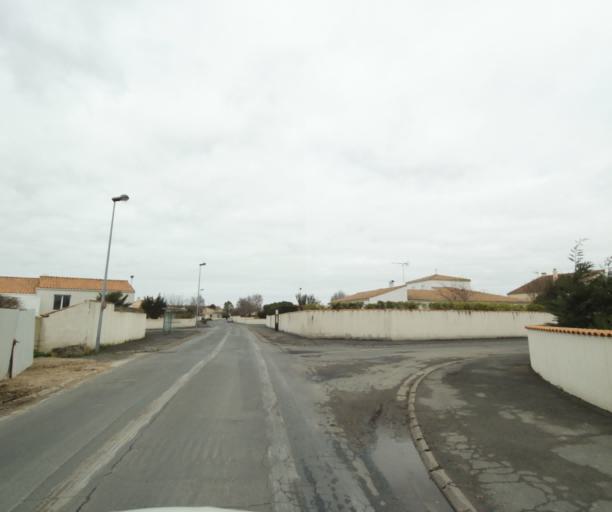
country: FR
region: Poitou-Charentes
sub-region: Departement de la Charente-Maritime
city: Lagord
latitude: 46.1926
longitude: -1.1533
